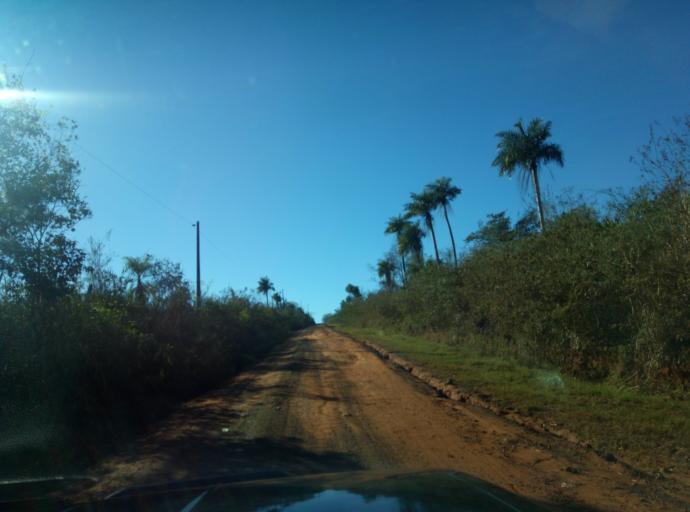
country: PY
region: Caaguazu
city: Carayao
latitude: -25.1575
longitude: -56.2980
